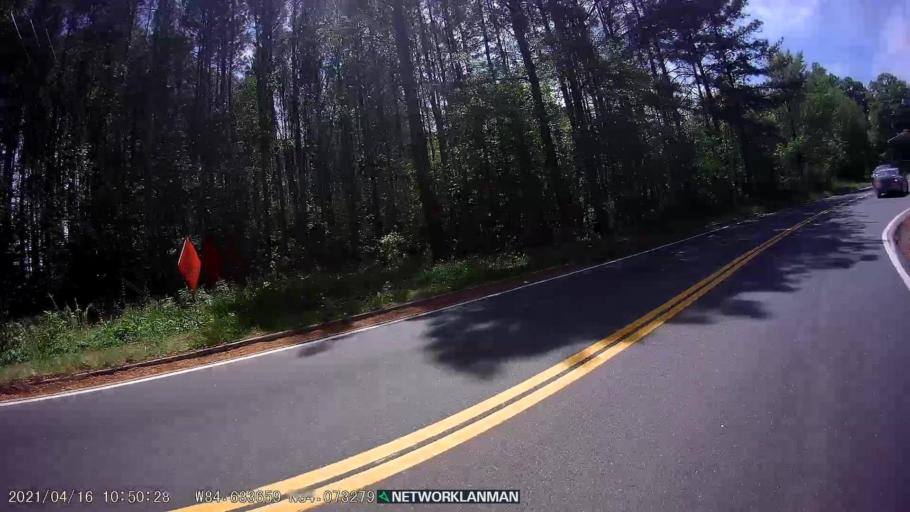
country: US
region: Georgia
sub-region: Cobb County
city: Acworth
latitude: 34.0731
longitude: -84.6338
